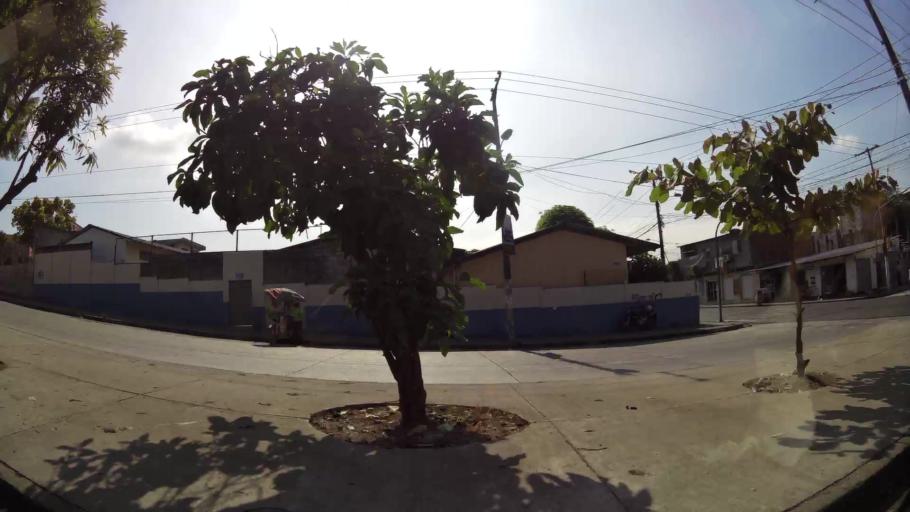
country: EC
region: Guayas
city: Eloy Alfaro
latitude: -2.1748
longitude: -79.8048
